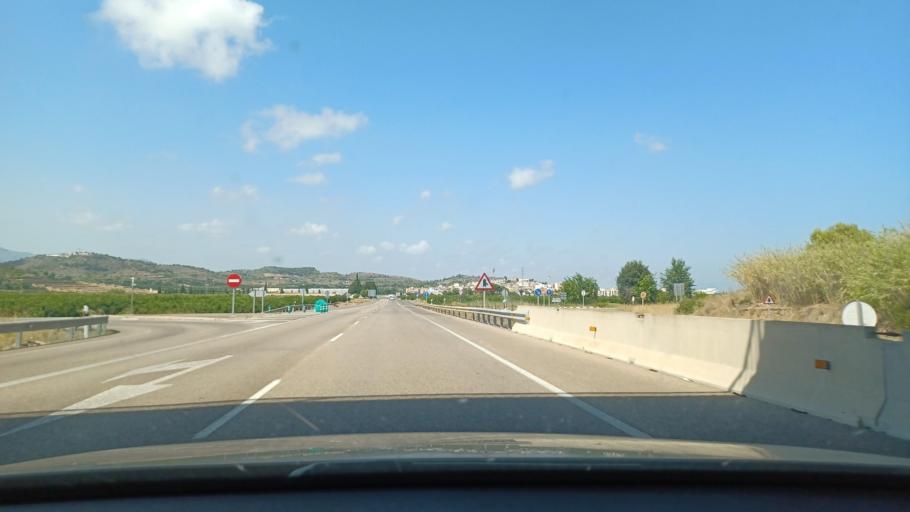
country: ES
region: Valencia
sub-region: Provincia de Castello
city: Almenara
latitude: 39.7593
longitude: -0.2125
